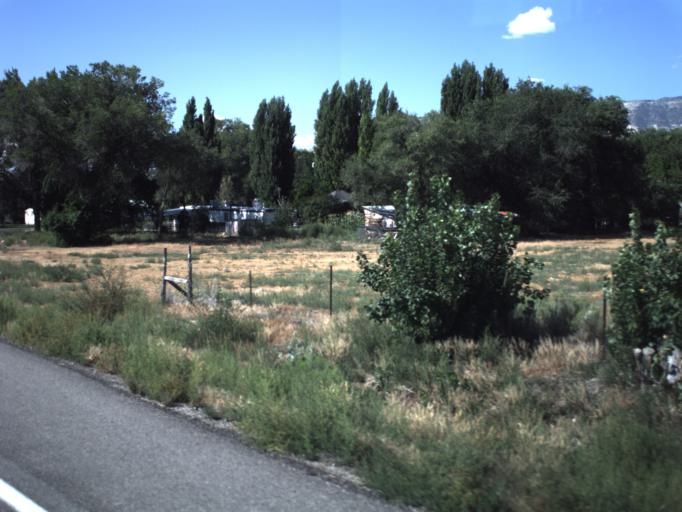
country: US
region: Utah
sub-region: Emery County
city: Ferron
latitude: 39.0962
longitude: -111.1322
